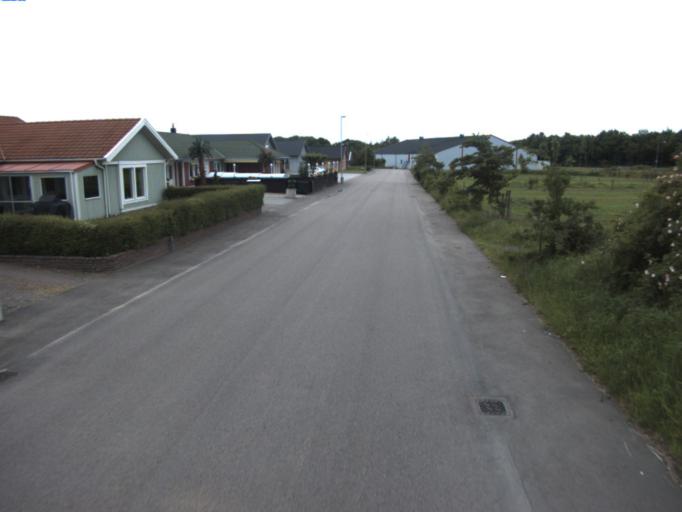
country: SE
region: Skane
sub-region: Helsingborg
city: Odakra
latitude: 56.1091
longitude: 12.7551
